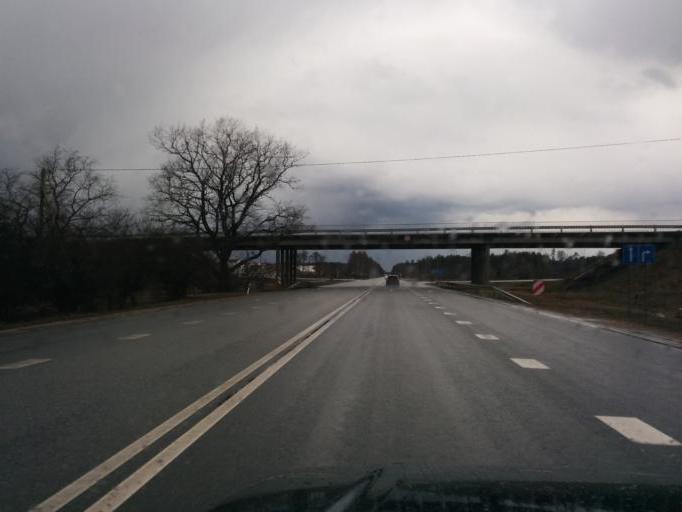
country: LV
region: Babite
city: Pinki
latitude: 56.8770
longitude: 23.9547
